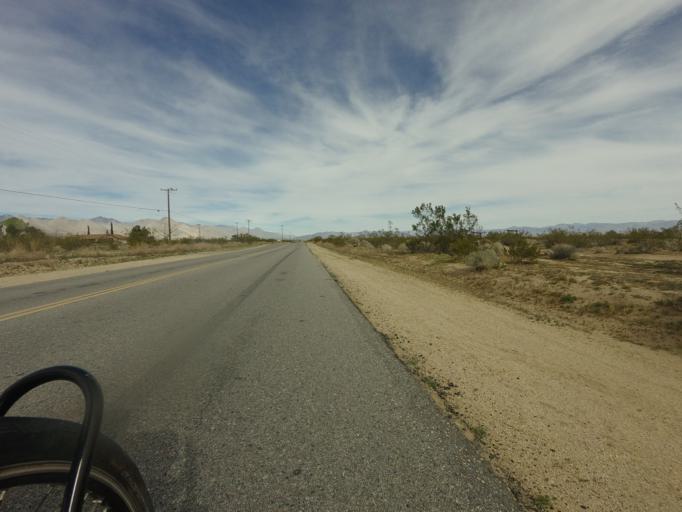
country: US
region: California
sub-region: Kern County
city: Inyokern
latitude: 35.6908
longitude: -117.8253
